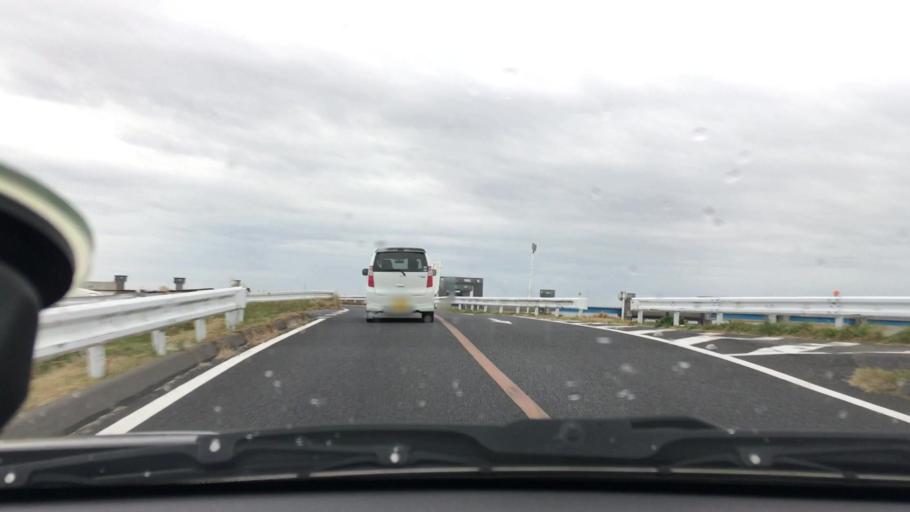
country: JP
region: Chiba
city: Omigawa
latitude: 35.8428
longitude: 140.7019
